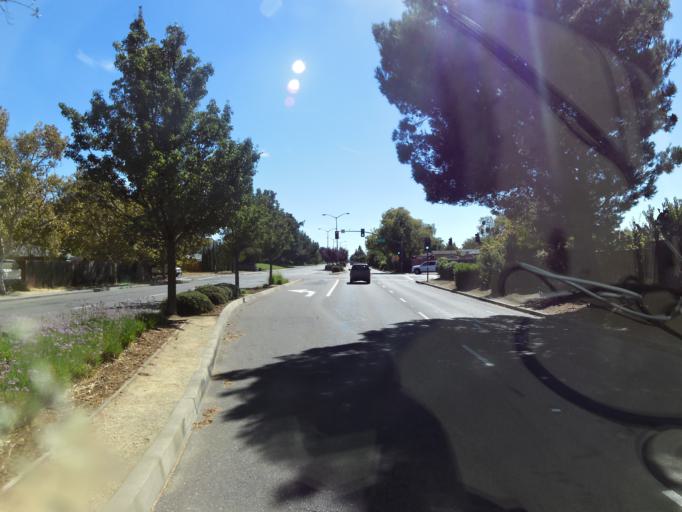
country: US
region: California
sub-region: Solano County
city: Fairfield
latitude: 38.2551
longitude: -122.0499
